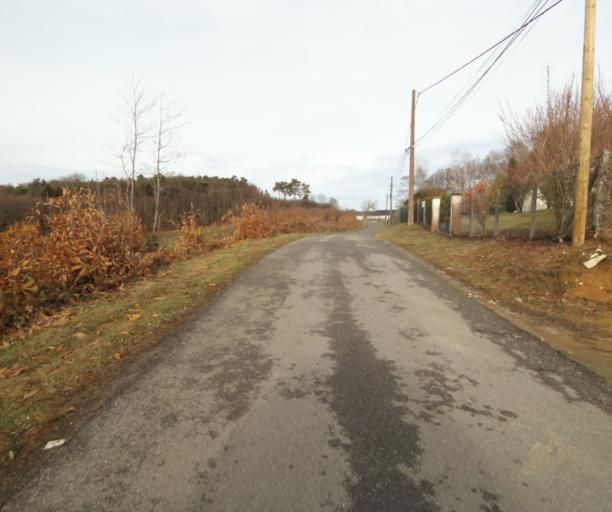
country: FR
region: Limousin
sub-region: Departement de la Correze
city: Saint-Mexant
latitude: 45.2747
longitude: 1.6813
